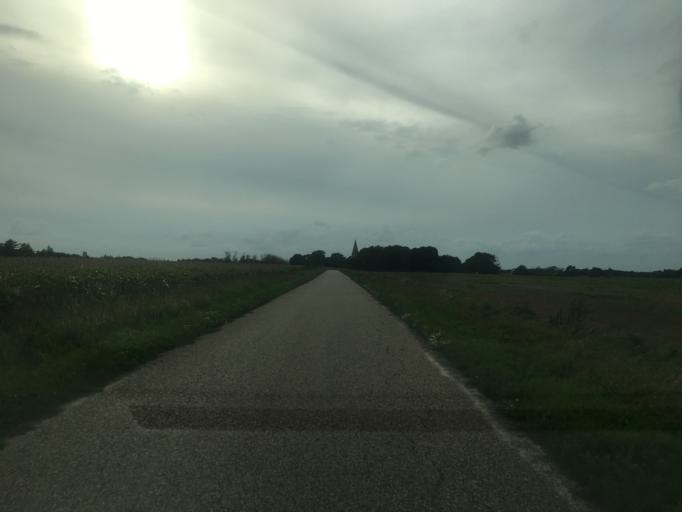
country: DE
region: Schleswig-Holstein
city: Aventoft
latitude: 54.9697
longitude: 8.7546
